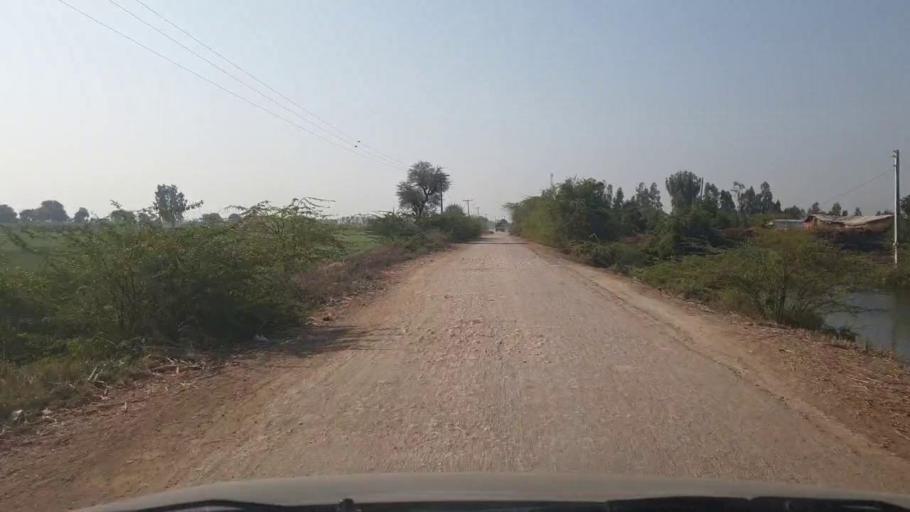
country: PK
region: Sindh
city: Mirwah Gorchani
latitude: 25.3016
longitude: 69.1485
